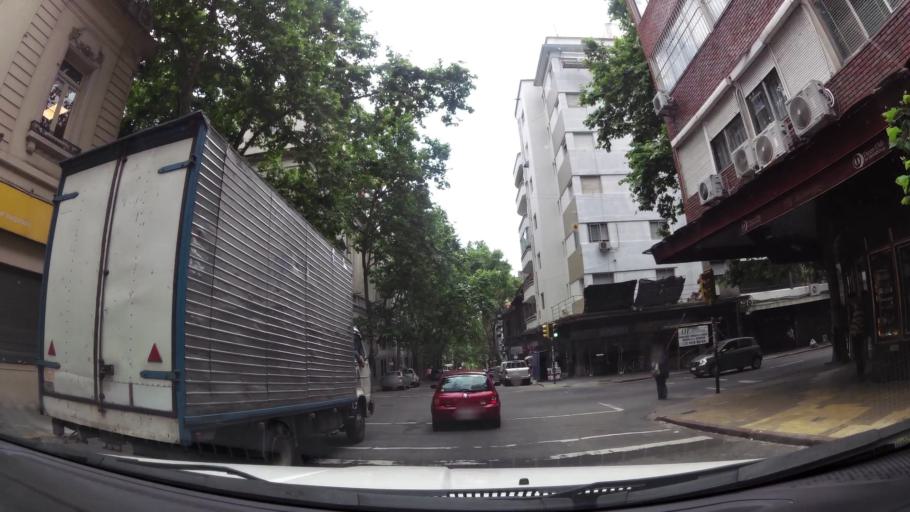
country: UY
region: Montevideo
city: Montevideo
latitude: -34.9051
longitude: -56.1926
